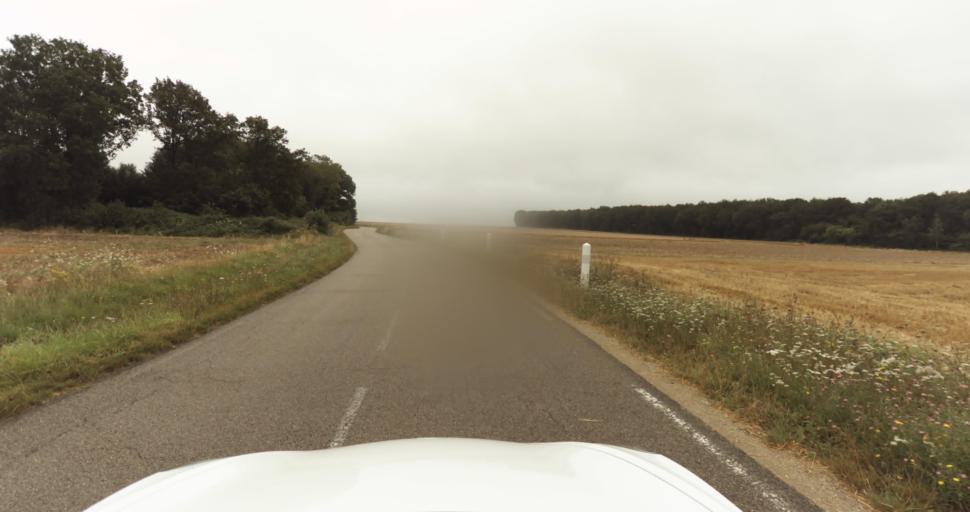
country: FR
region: Haute-Normandie
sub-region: Departement de l'Eure
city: Normanville
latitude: 49.0926
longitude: 1.1696
